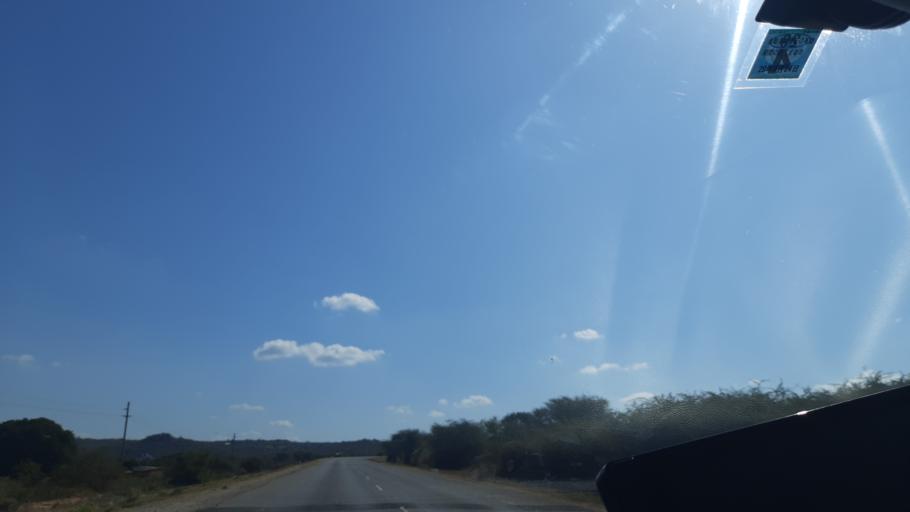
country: TZ
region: Singida
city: Kilimatinde
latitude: -5.7826
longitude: 34.8905
